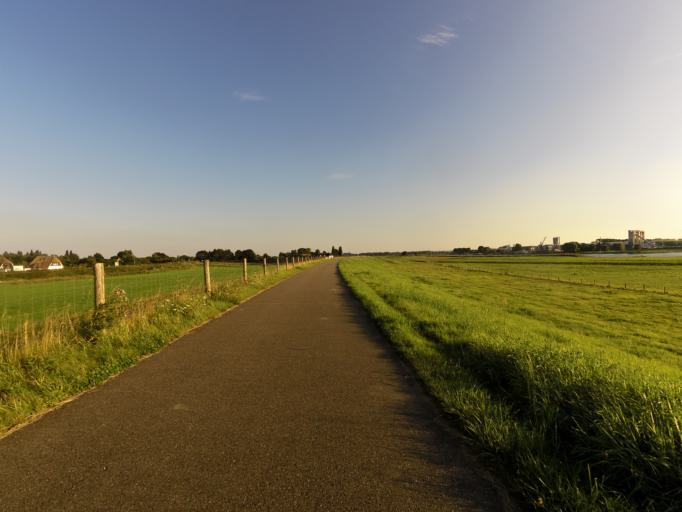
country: NL
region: Gelderland
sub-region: Gemeente Westervoort
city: Westervoort
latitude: 51.9449
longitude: 5.9650
